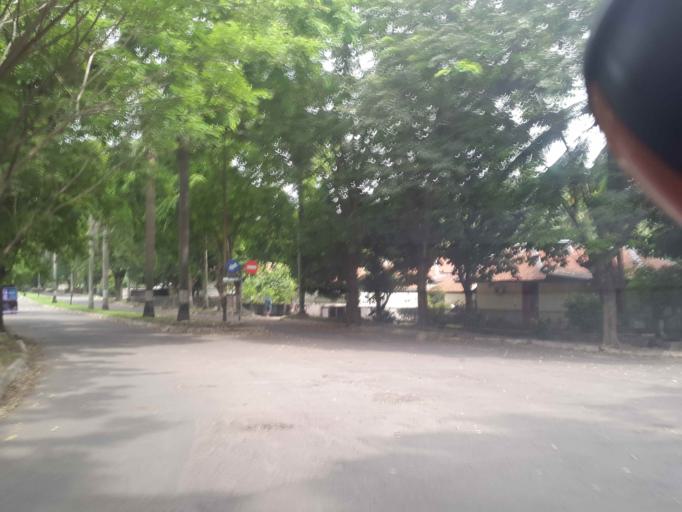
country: ID
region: Banten
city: Curug
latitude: -5.9912
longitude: 106.0409
